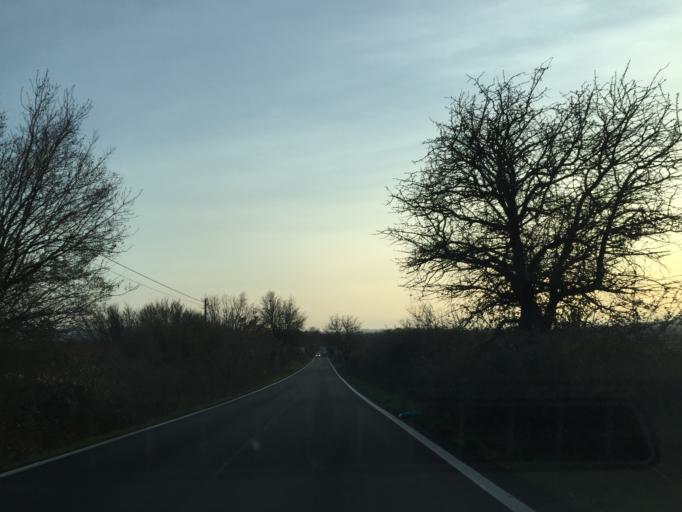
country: IT
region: Latium
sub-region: Citta metropolitana di Roma Capitale
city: Campagnano di Roma
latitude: 42.1769
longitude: 12.3602
